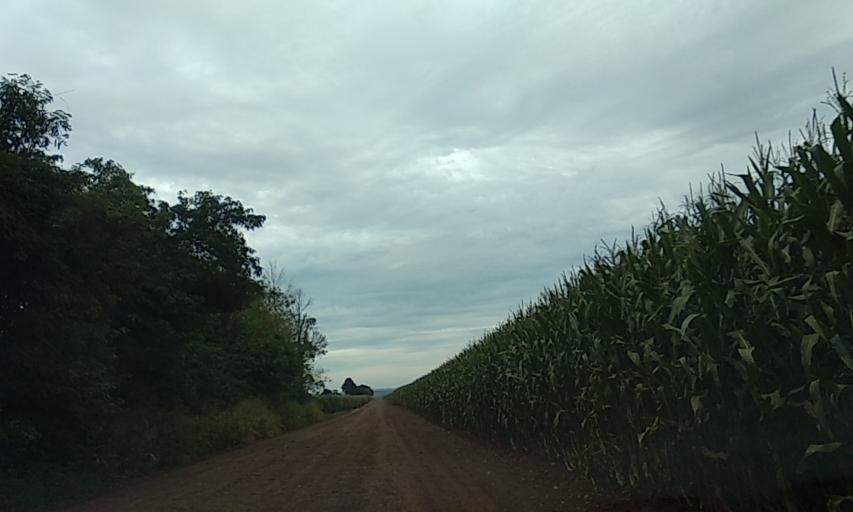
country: BR
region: Parana
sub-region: Marechal Candido Rondon
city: Marechal Candido Rondon
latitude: -24.5404
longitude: -54.0945
